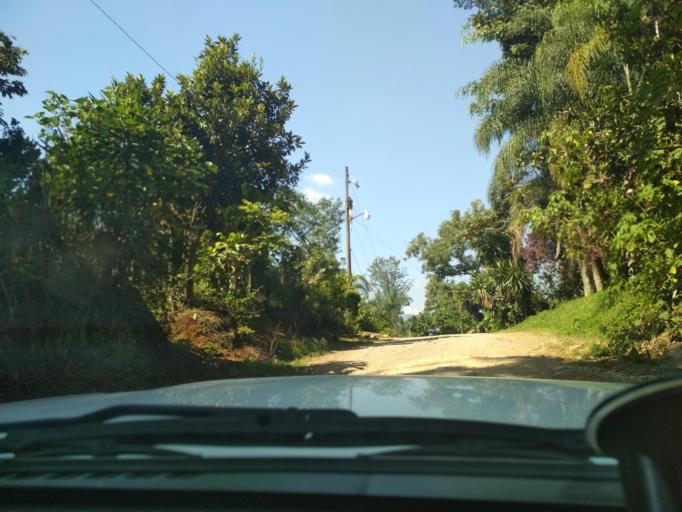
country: MX
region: Veracruz
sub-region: Fortin
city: Fraccionamiento los Alamos
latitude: 18.9196
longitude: -96.9809
